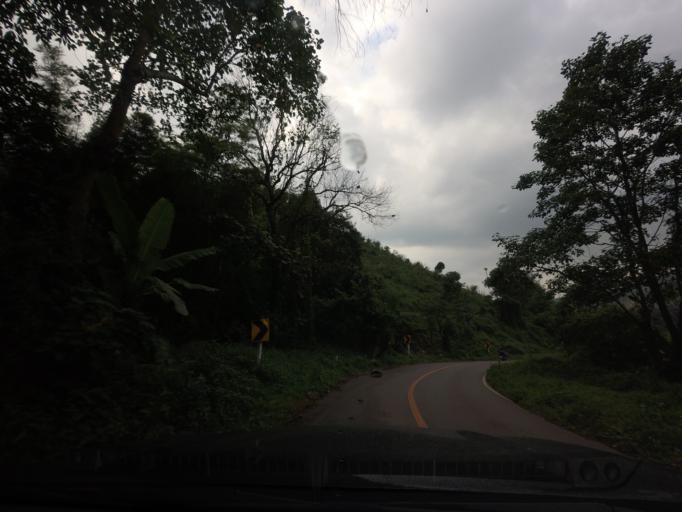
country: TH
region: Nan
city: Bo Kluea
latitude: 19.3200
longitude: 101.1721
